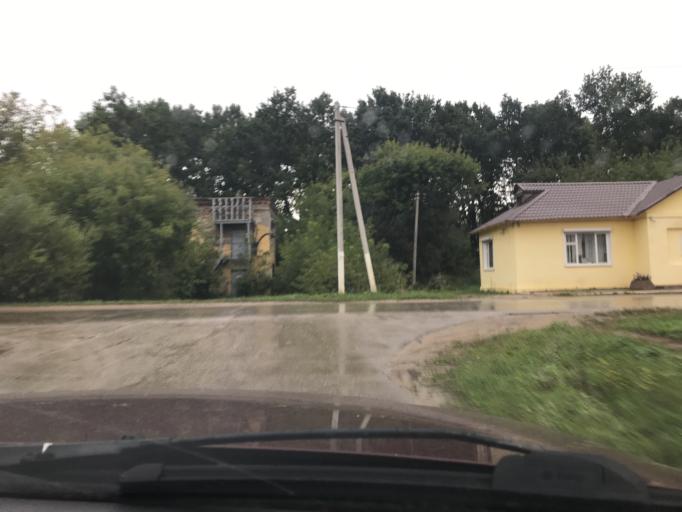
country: RU
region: Kaluga
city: Pyatovskiy
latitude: 54.6903
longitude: 36.0568
